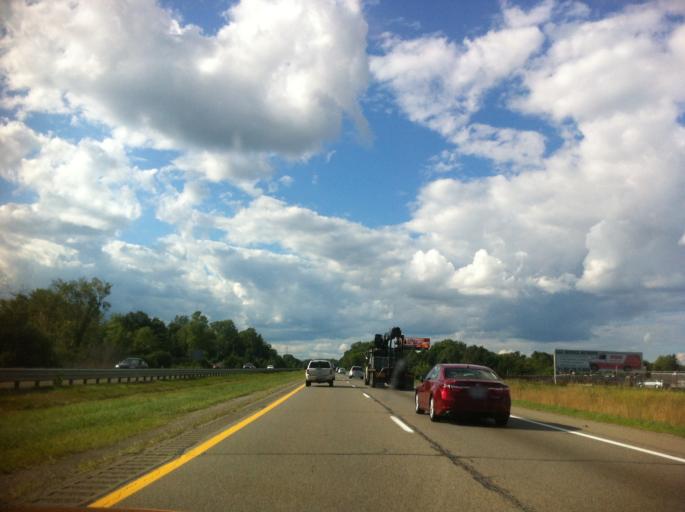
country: US
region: Michigan
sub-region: Livingston County
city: Whitmore Lake
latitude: 42.4109
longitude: -83.7635
